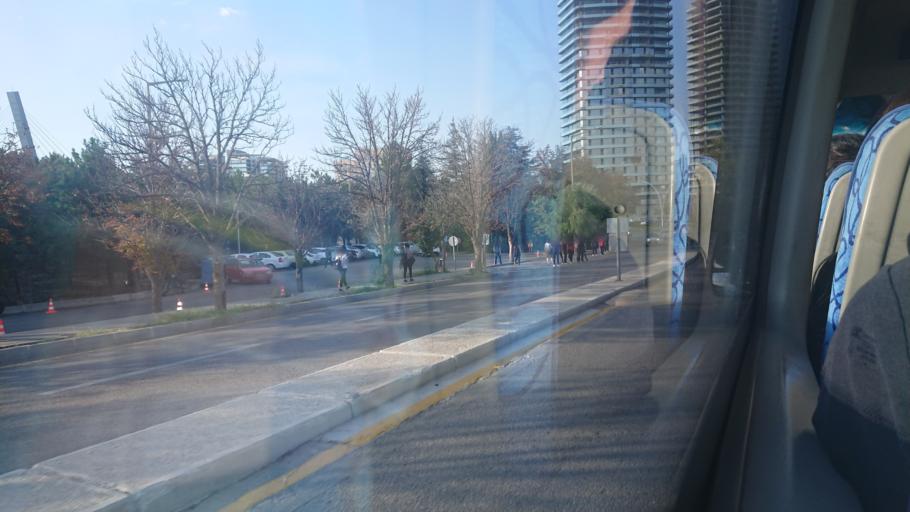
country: TR
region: Ankara
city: Ankara
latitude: 39.9069
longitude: 32.7840
